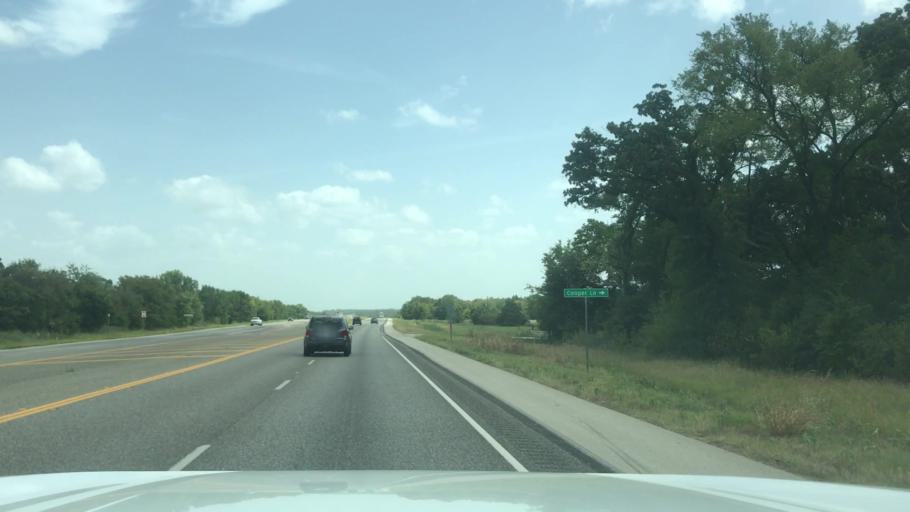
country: US
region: Texas
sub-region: Robertson County
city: Calvert
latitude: 30.9606
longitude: -96.6590
